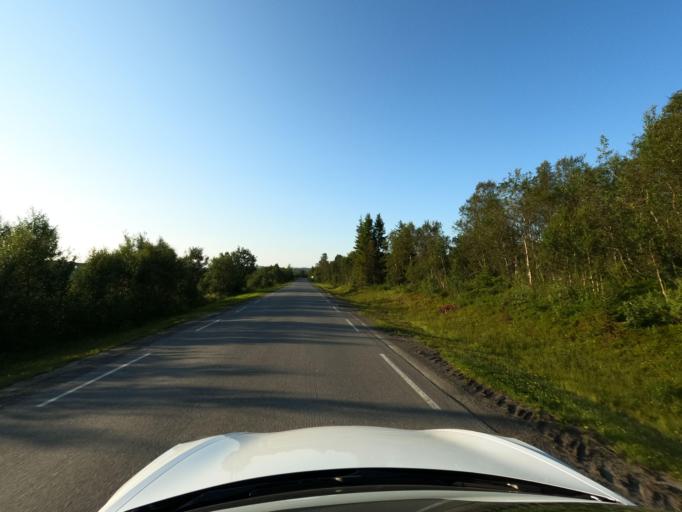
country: NO
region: Troms
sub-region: Skanland
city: Evenskjer
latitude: 68.4813
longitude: 16.7112
